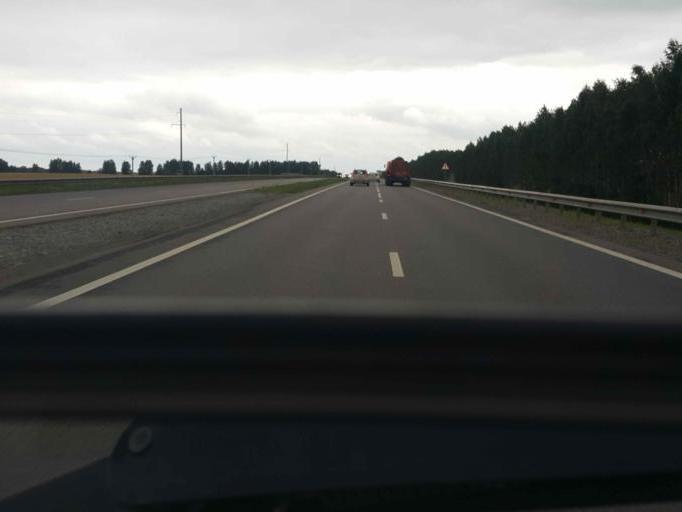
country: RU
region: Tambov
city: Zavoronezhskoye
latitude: 52.8785
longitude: 40.7441
